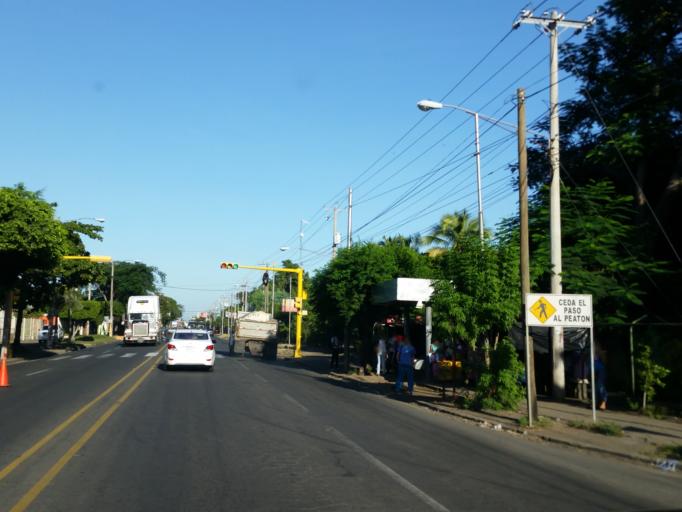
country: NI
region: Managua
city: Ciudad Sandino
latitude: 12.1513
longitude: -86.3108
